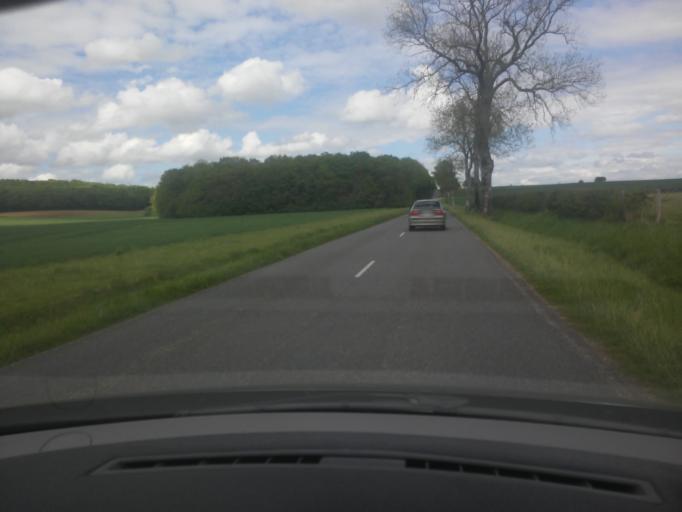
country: FR
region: Lorraine
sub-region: Departement de Meurthe-et-Moselle
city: Longuyon
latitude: 49.3879
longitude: 5.6007
